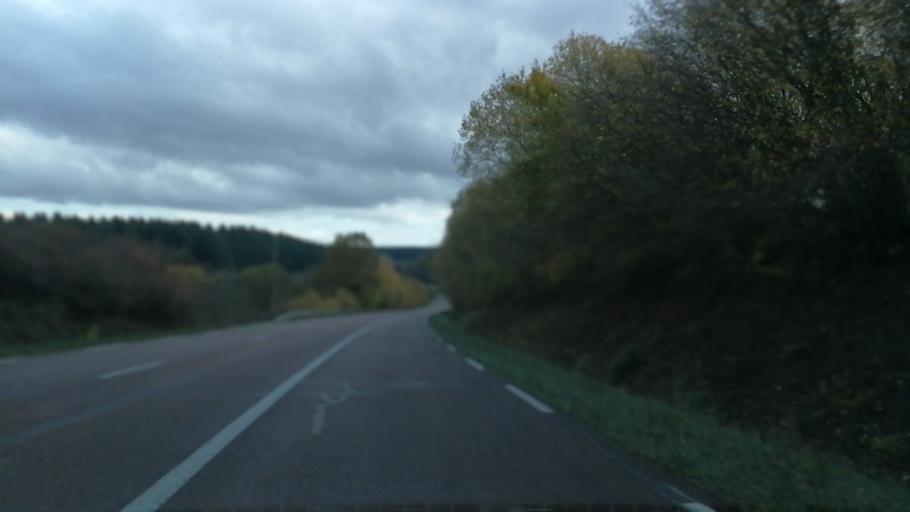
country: FR
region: Bourgogne
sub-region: Departement de la Cote-d'Or
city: Saulieu
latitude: 47.2613
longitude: 4.2649
